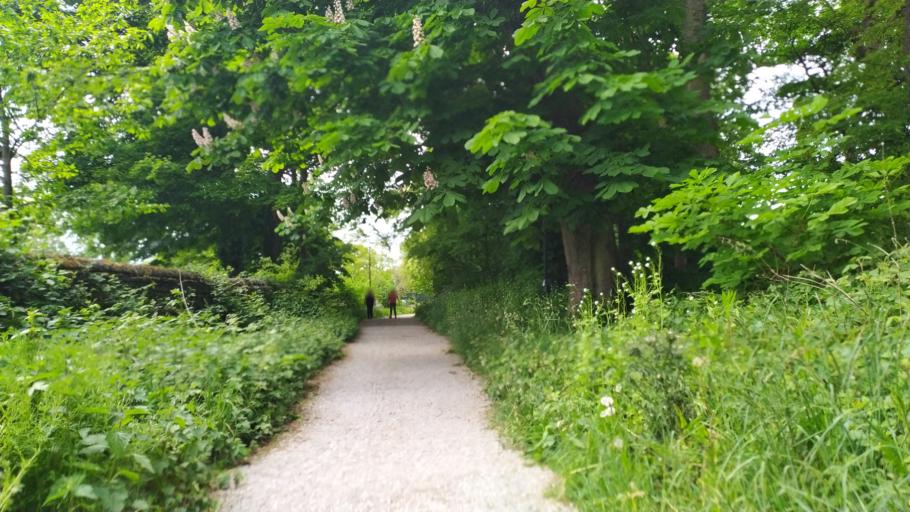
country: GB
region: England
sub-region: City and Borough of Leeds
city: Chapel Allerton
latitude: 53.8362
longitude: -1.5875
